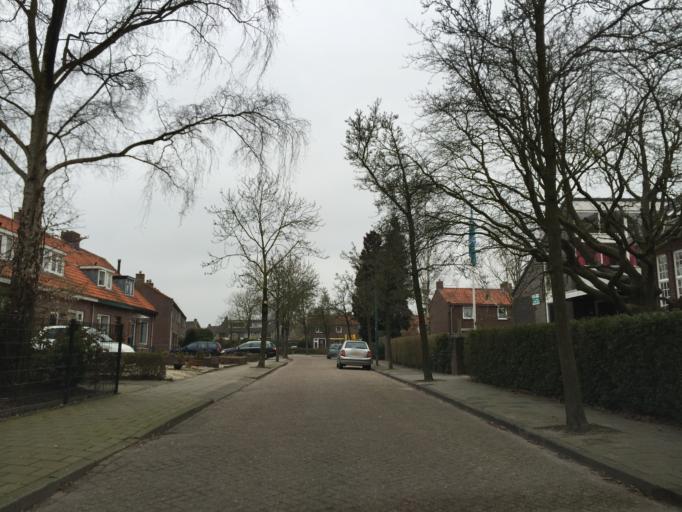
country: NL
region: Utrecht
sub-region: Stichtse Vecht
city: Maarssen
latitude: 52.0841
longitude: 5.0403
